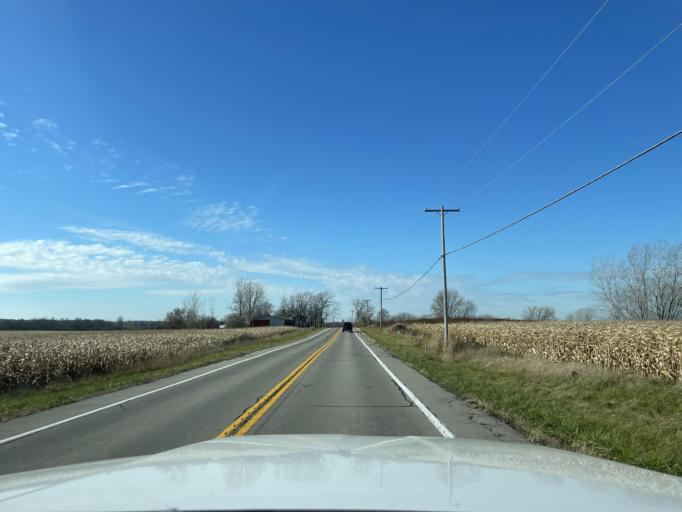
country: US
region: New York
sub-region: Niagara County
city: Middleport
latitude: 43.2155
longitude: -78.4543
